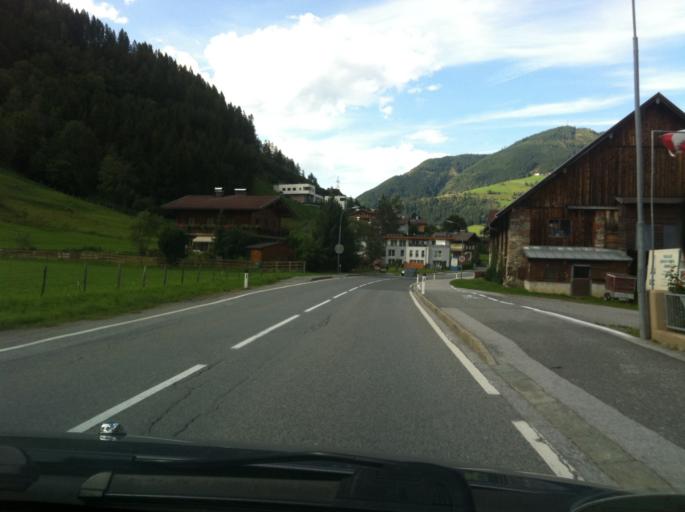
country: AT
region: Salzburg
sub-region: Politischer Bezirk Zell am See
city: Bruck an der Grossglocknerstrasse
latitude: 47.2697
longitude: 12.8250
